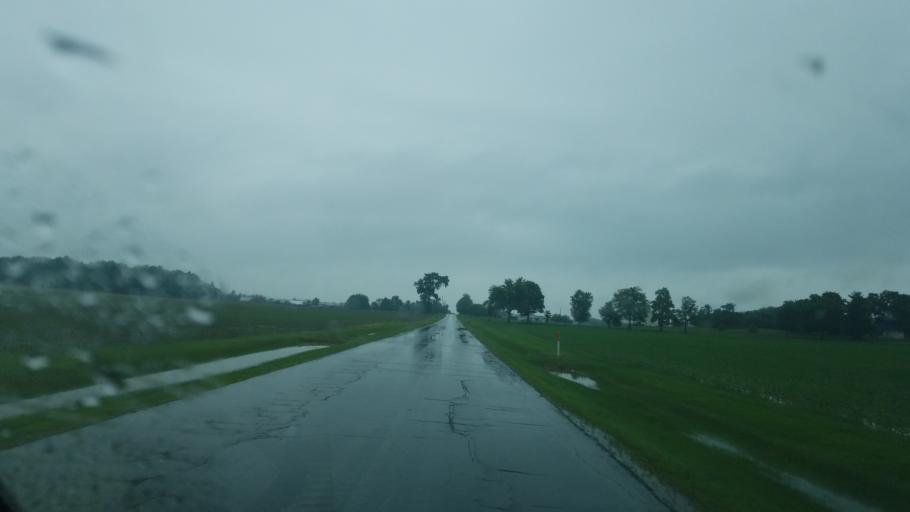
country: US
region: Ohio
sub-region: Huron County
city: Plymouth
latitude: 40.9843
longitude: -82.6056
